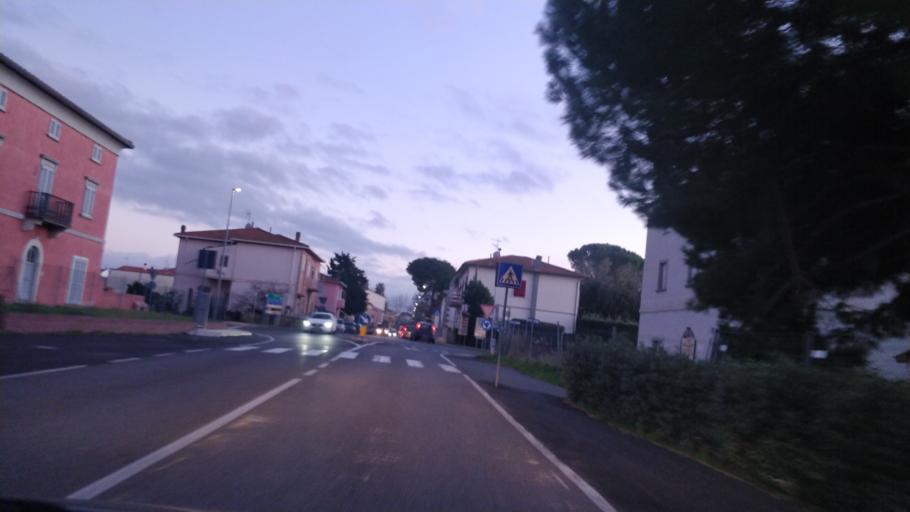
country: IT
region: Tuscany
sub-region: Provincia di Livorno
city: Vada
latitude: 43.3544
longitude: 10.4557
